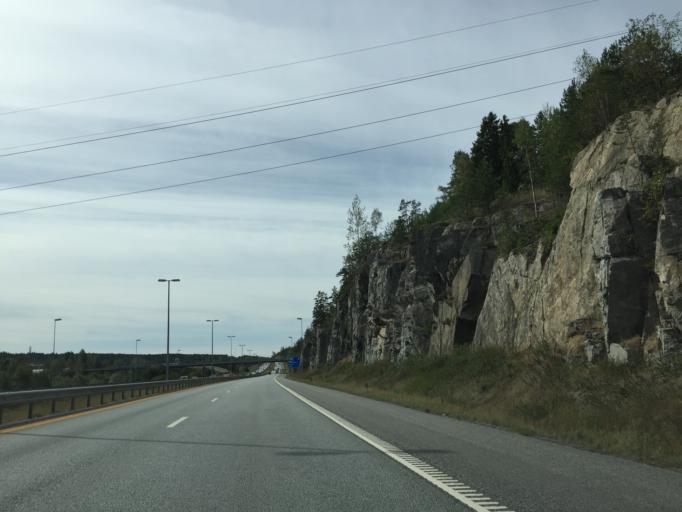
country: NO
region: Akershus
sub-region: Vestby
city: Vestby
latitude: 59.5208
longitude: 10.7275
